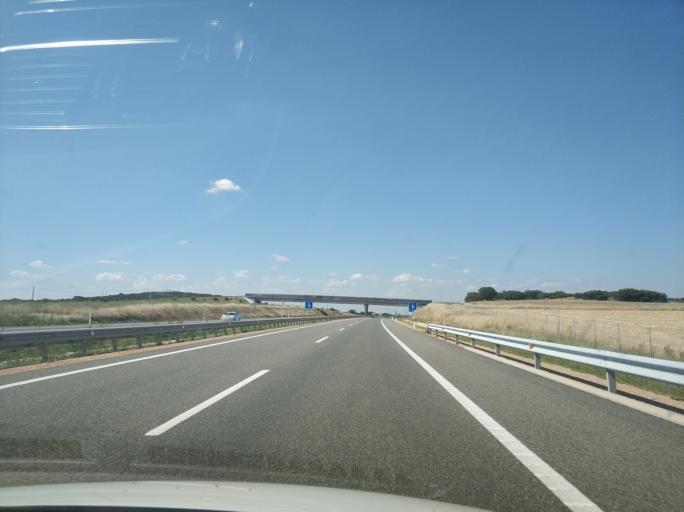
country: ES
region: Castille and Leon
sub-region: Provincia de Zamora
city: Montamarta
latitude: 41.6796
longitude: -5.8051
